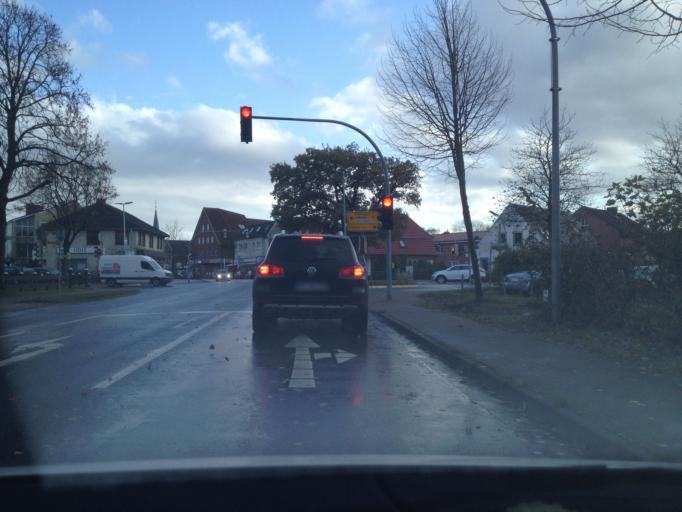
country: DE
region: Schleswig-Holstein
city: Leck
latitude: 54.7740
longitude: 8.9686
